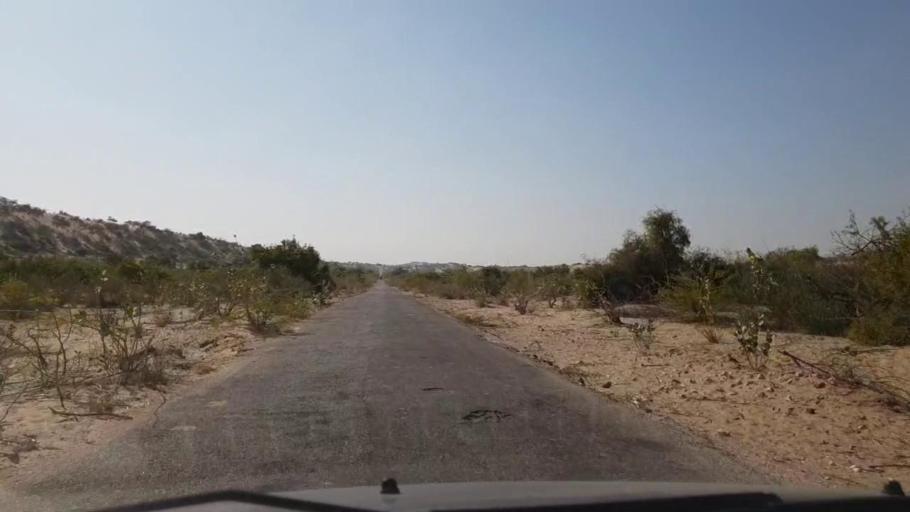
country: PK
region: Sindh
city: Diplo
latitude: 24.5335
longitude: 69.6358
